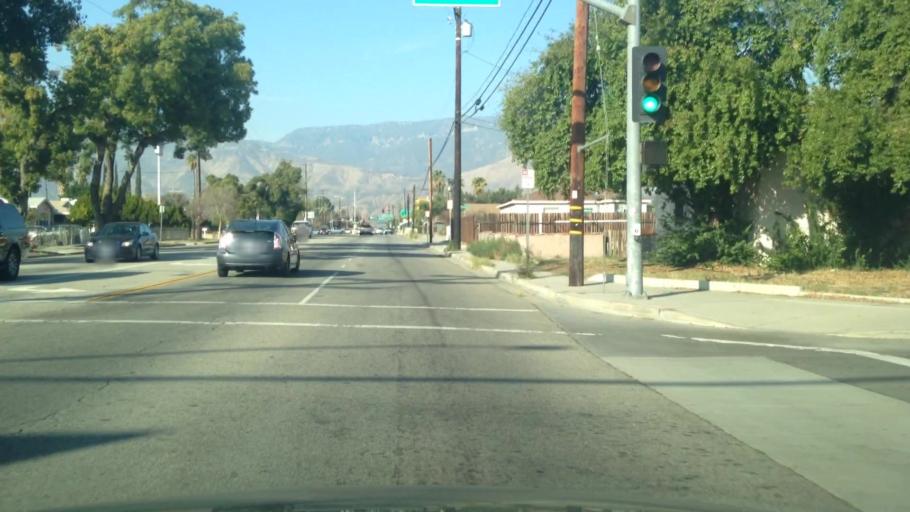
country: US
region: California
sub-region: San Bernardino County
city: San Bernardino
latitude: 34.1423
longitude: -117.2786
